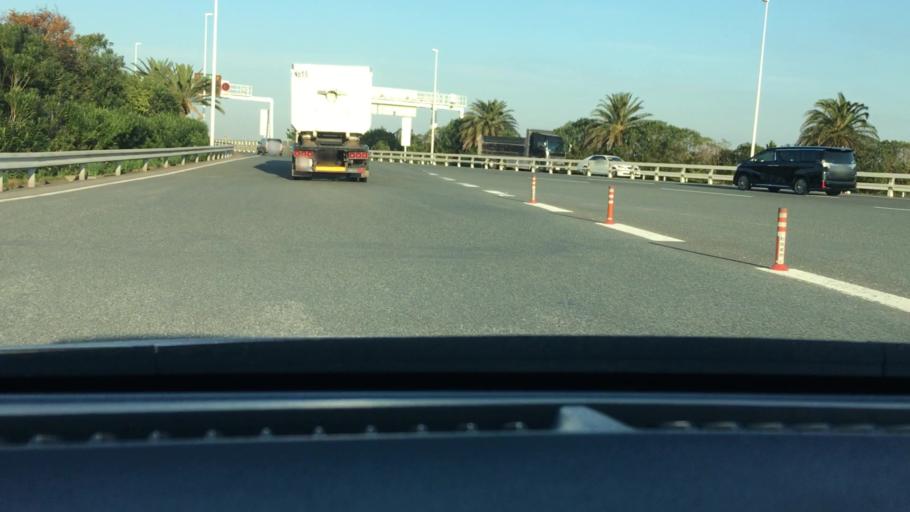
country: JP
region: Chiba
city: Kisarazu
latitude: 35.4360
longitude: 139.9175
